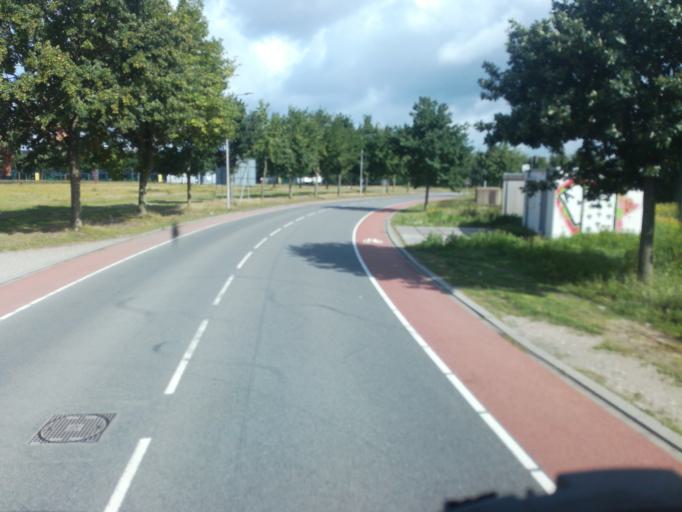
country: NL
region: Limburg
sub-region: Gemeente Peel en Maas
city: Maasbree
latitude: 51.3899
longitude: 6.0944
